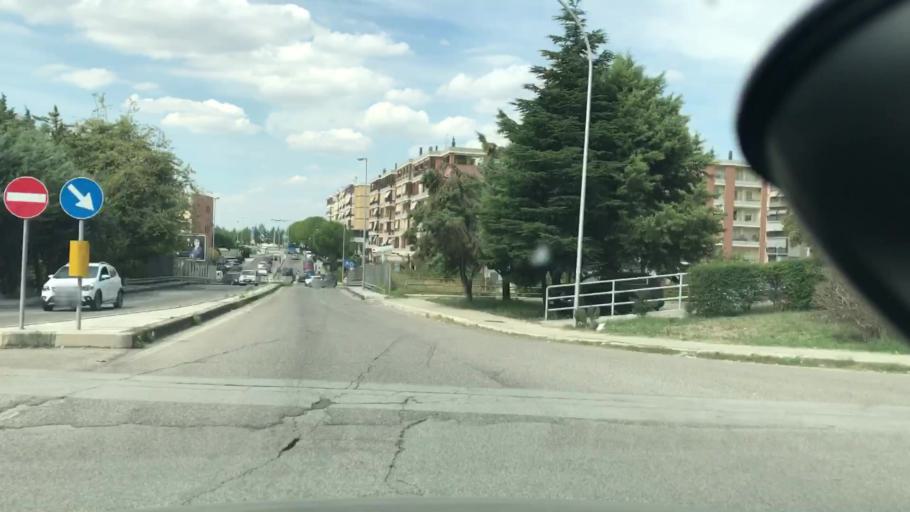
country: IT
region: Basilicate
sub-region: Provincia di Matera
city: Matera
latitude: 40.6767
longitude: 16.5830
